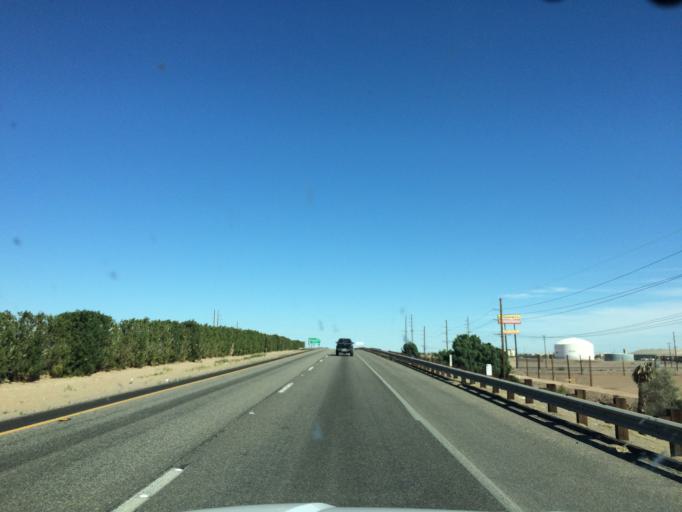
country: US
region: California
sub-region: Imperial County
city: El Centro
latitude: 32.7737
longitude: -115.5463
